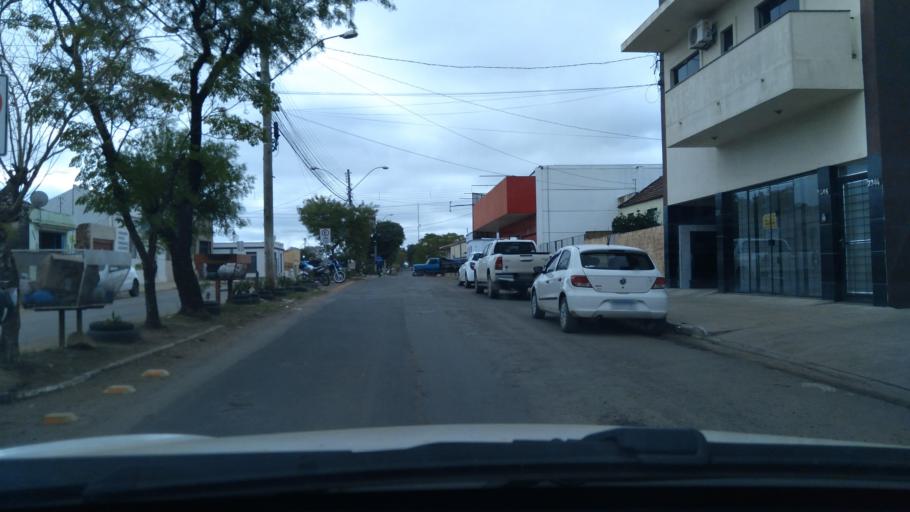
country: BR
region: Rio Grande do Sul
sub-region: Dom Pedrito
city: Dom Pedrito
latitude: -30.9726
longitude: -54.6737
